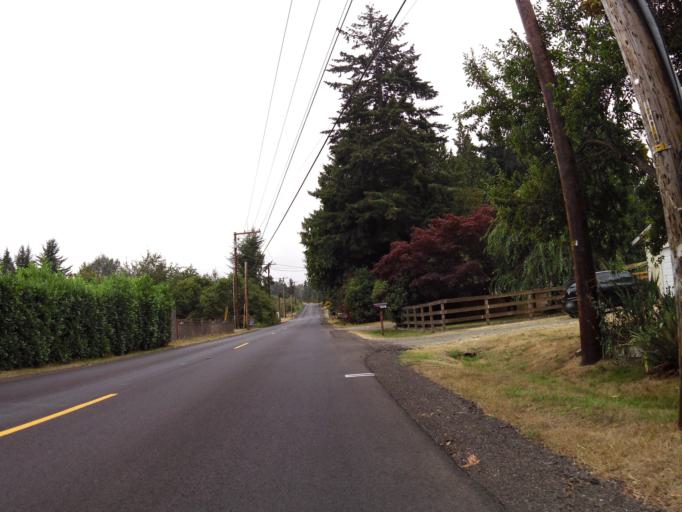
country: US
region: Washington
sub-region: Kitsap County
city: Lofall
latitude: 47.8047
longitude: -122.6600
